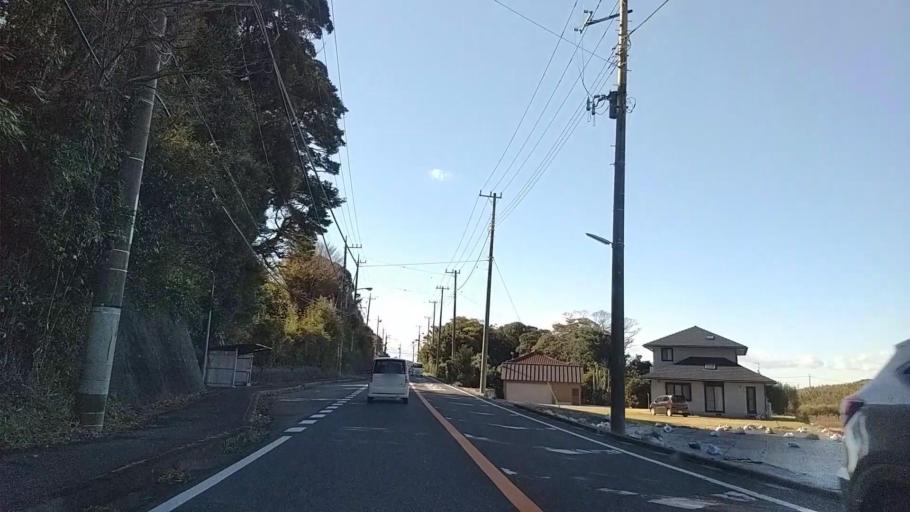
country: JP
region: Chiba
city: Tateyama
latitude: 34.9508
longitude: 139.8366
